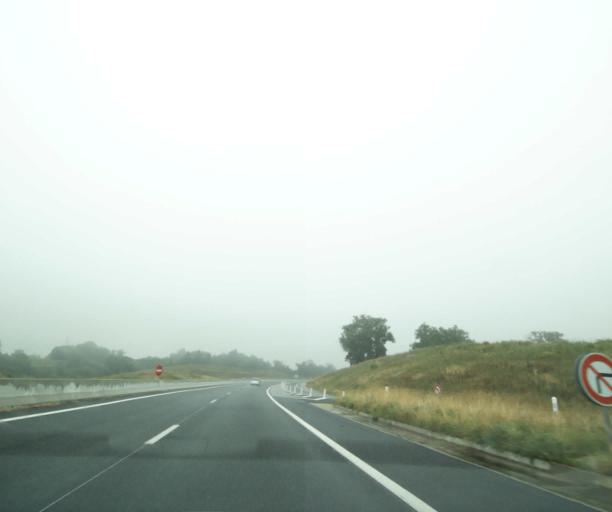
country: FR
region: Midi-Pyrenees
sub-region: Departement de l'Aveyron
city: Naucelle
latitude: 44.1886
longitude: 2.3574
